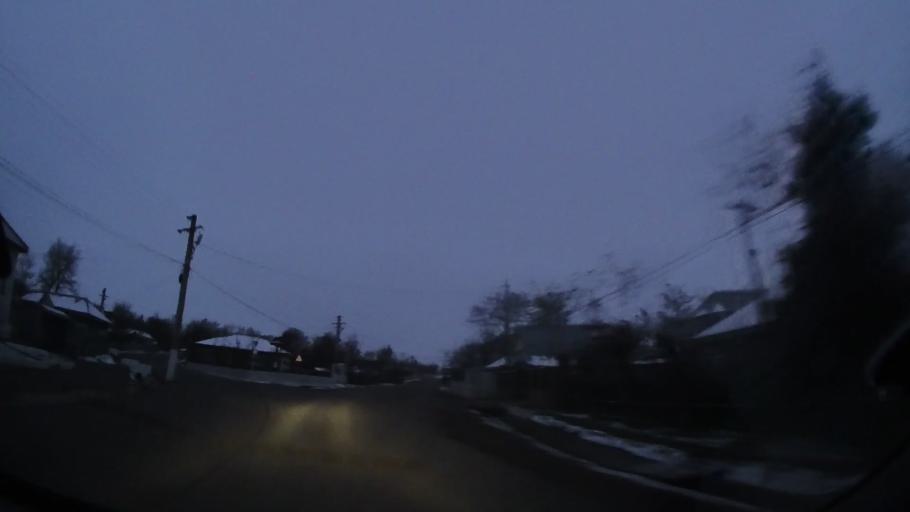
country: RO
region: Vaslui
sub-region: Comuna Dimitrie Cantemir
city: Dimitrie Cantemir
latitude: 46.5065
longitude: 28.0554
